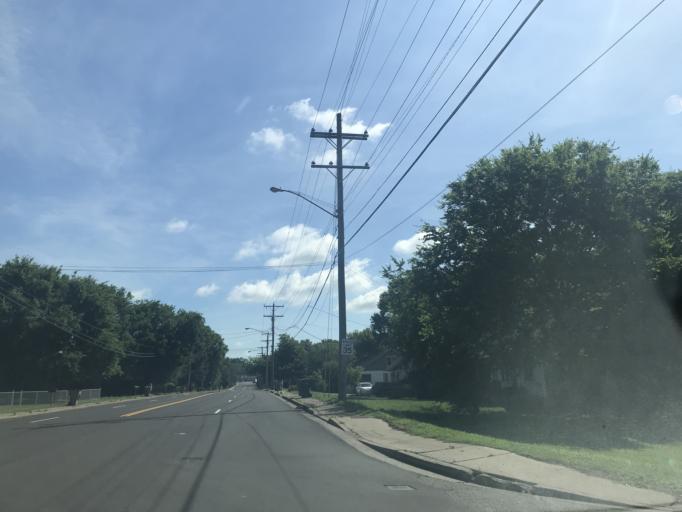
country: US
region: Tennessee
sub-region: Davidson County
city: Nashville
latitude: 36.1893
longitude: -86.8378
